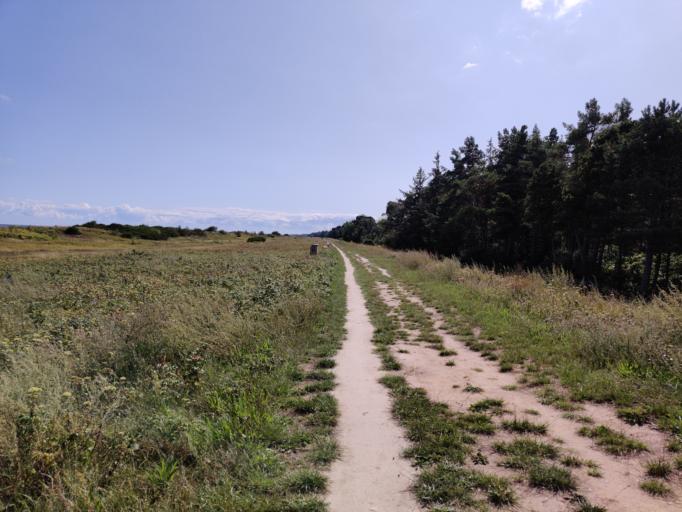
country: DK
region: Zealand
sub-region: Guldborgsund Kommune
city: Nykobing Falster
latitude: 54.6591
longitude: 11.9596
